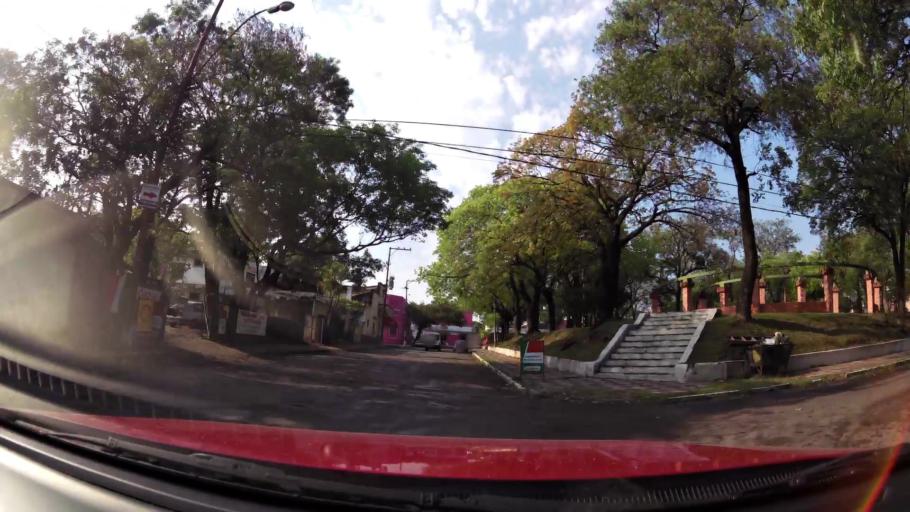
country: PY
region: Presidente Hayes
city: Nanawa
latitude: -25.2768
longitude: -57.6477
